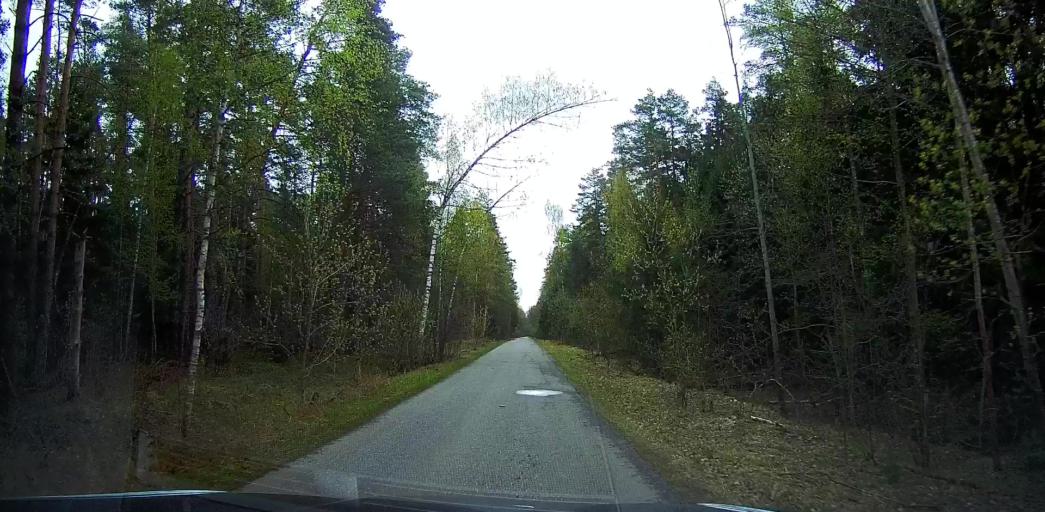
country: RU
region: Moskovskaya
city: Malyshevo
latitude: 55.5454
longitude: 38.3747
